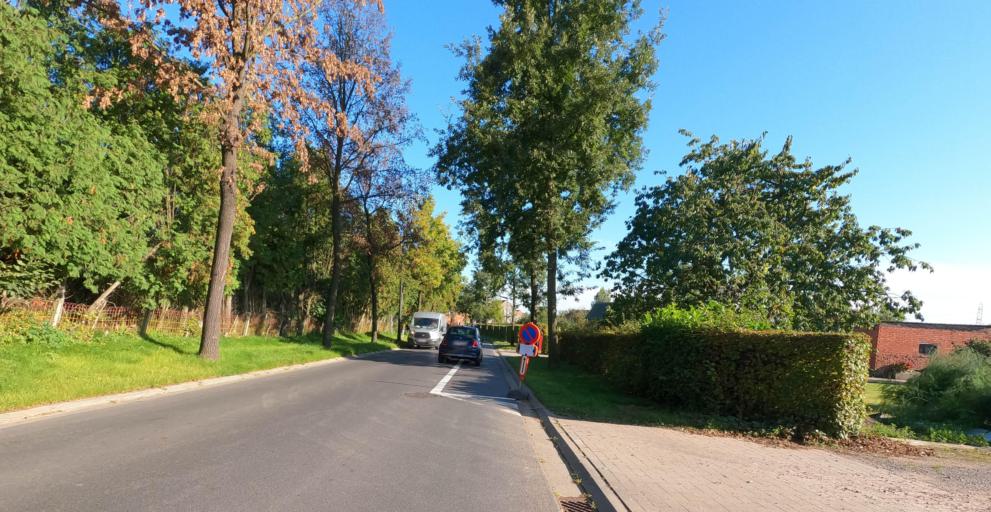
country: BE
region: Flanders
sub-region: Provincie Oost-Vlaanderen
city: Kruibeke
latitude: 51.1436
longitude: 4.2863
